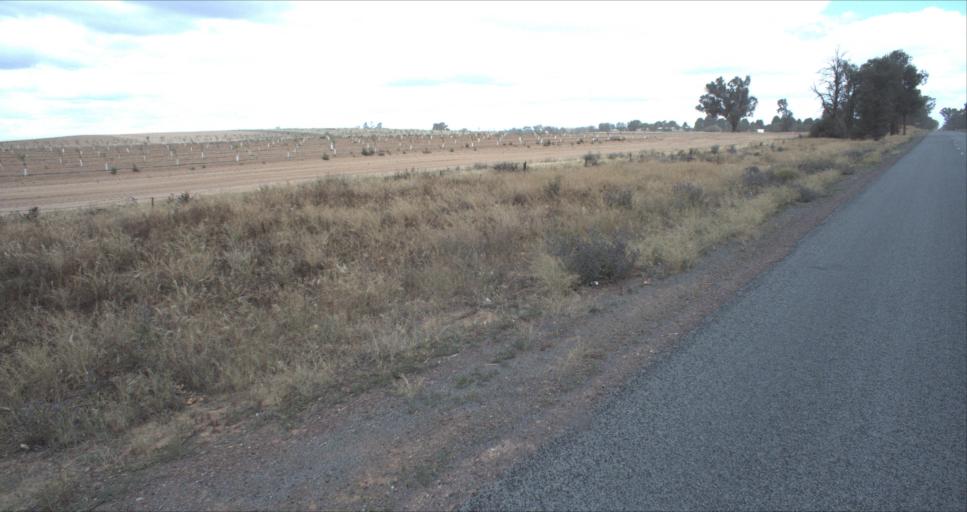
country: AU
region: New South Wales
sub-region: Leeton
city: Leeton
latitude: -34.6566
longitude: 146.3502
